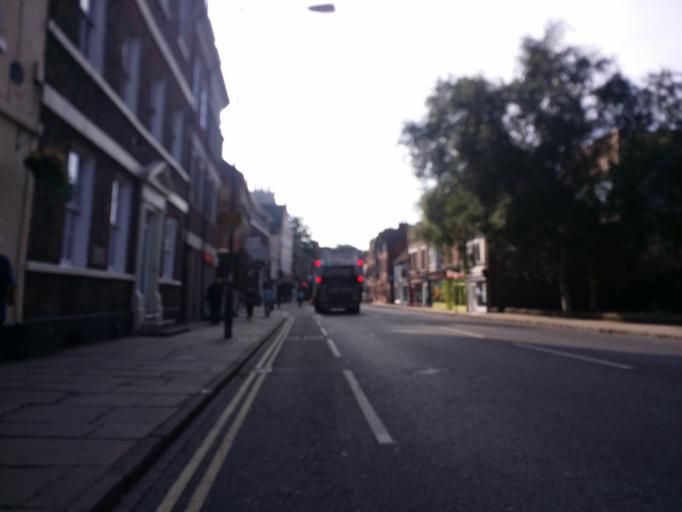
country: GB
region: England
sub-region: City of York
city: York
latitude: 53.9636
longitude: -1.0869
